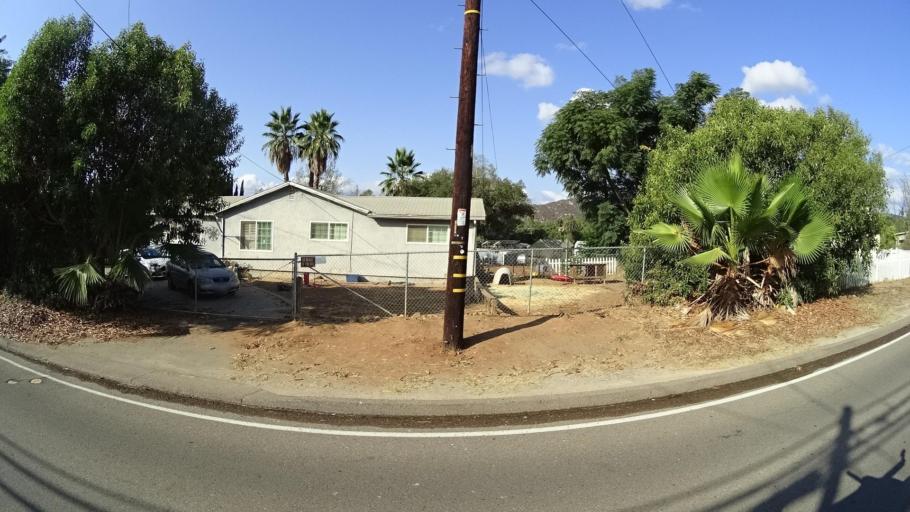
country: US
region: California
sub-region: San Diego County
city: Lakeside
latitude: 32.8694
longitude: -116.9328
